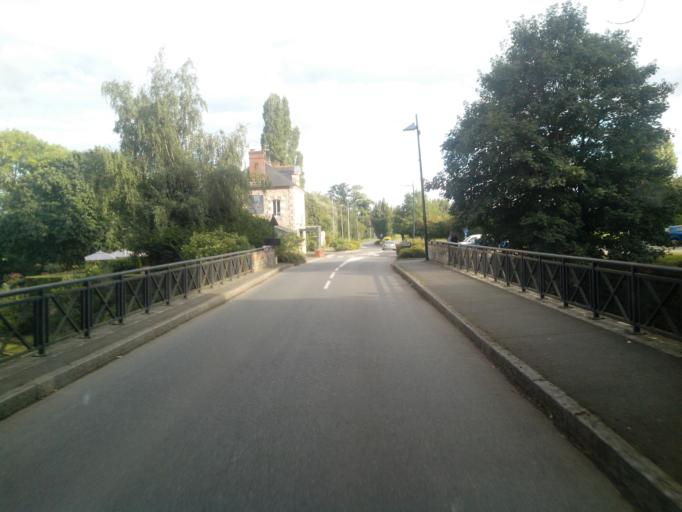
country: FR
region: Brittany
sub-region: Departement d'Ille-et-Vilaine
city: Acigne
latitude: 48.1311
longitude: -1.5353
